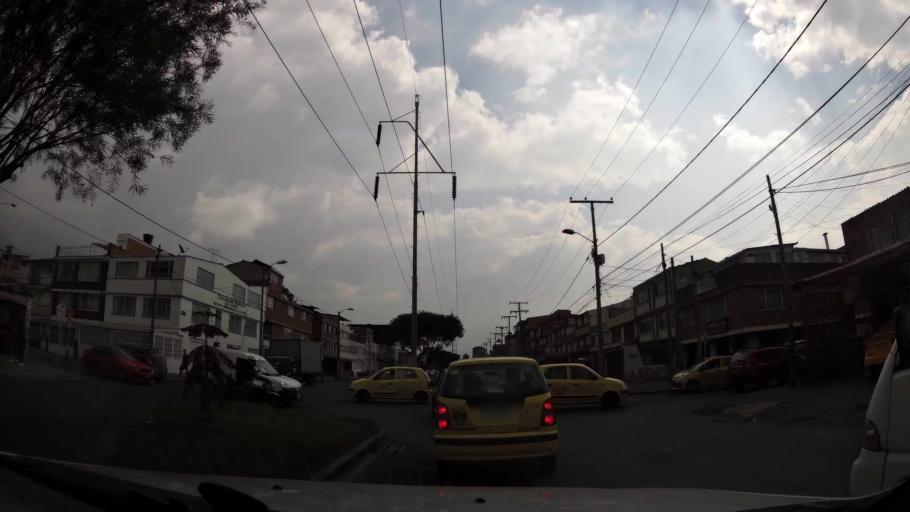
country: CO
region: Bogota D.C.
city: Bogota
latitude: 4.6041
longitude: -74.1101
